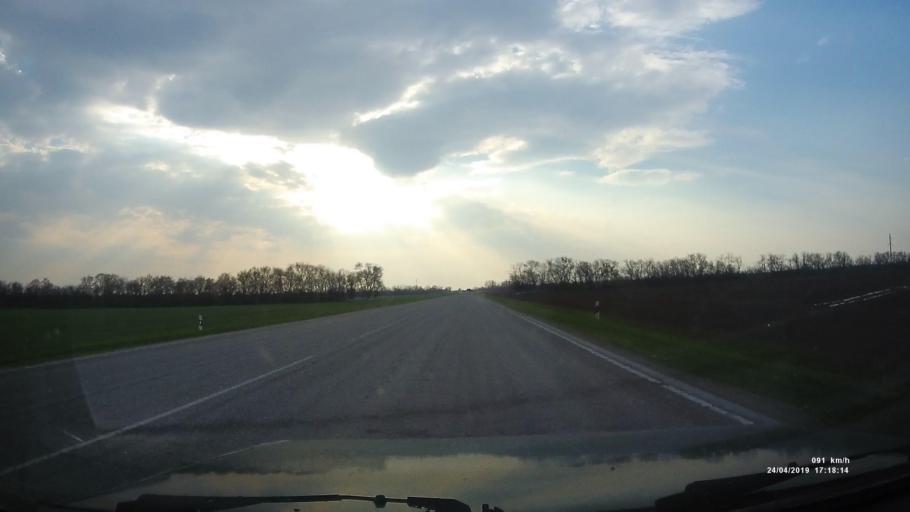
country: RU
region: Rostov
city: Gigant
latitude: 46.5111
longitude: 41.3898
